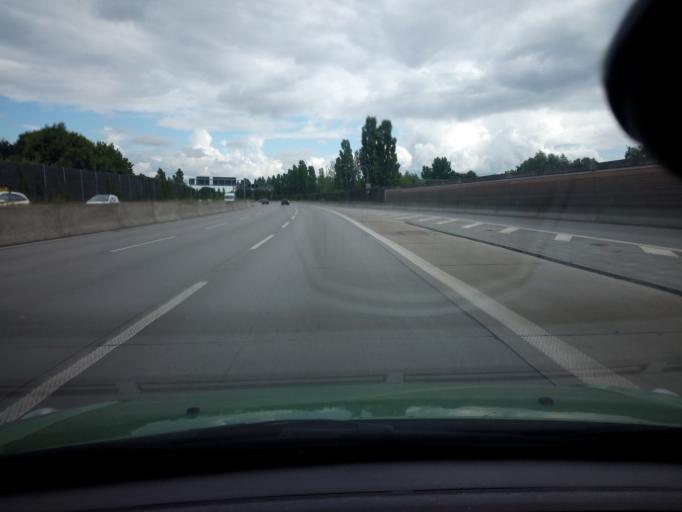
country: DE
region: Berlin
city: Buckow
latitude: 52.4526
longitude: 13.4621
